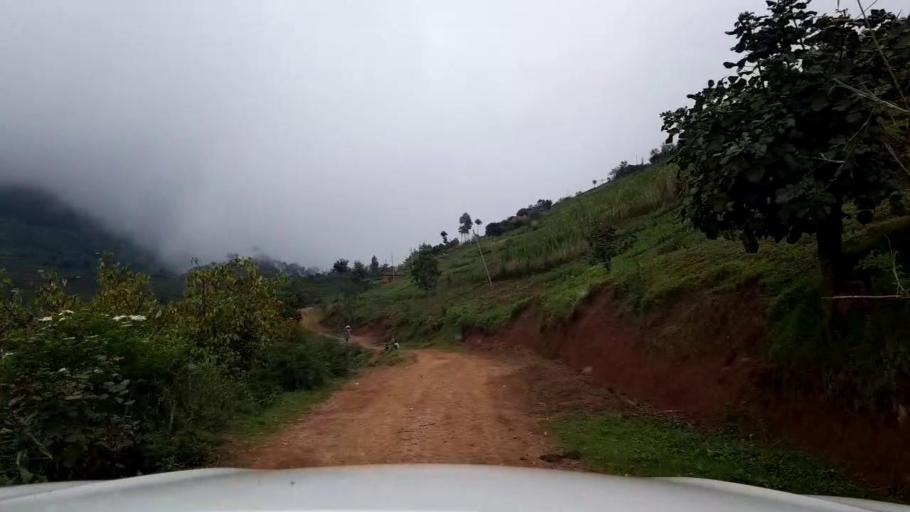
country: RW
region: Northern Province
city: Musanze
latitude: -1.5946
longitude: 29.7883
